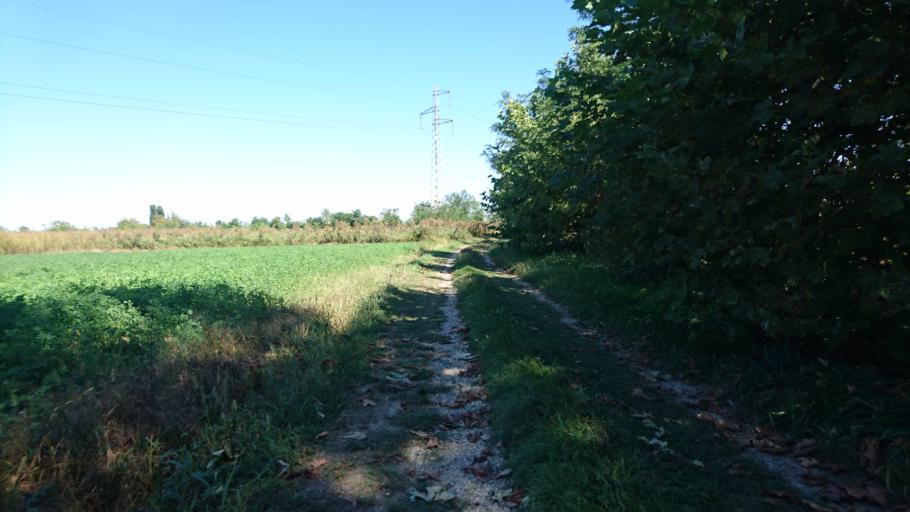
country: IT
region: Veneto
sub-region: Provincia di Venezia
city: Dolo
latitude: 45.4121
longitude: 12.0640
